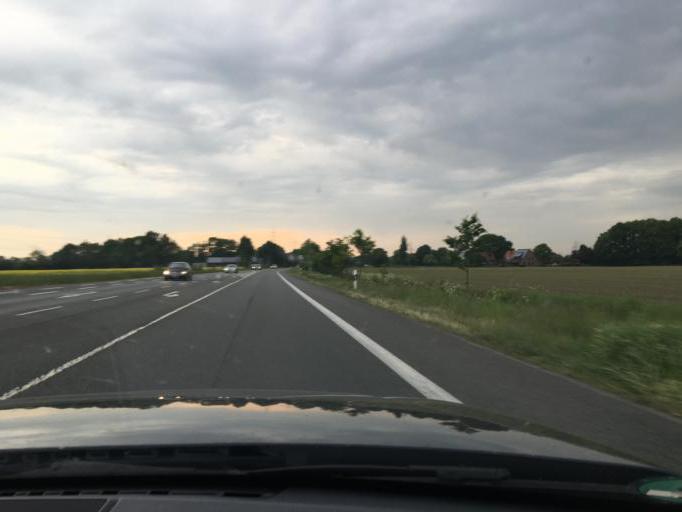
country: DE
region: North Rhine-Westphalia
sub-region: Regierungsbezirk Munster
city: Greven
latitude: 52.1280
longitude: 7.5819
